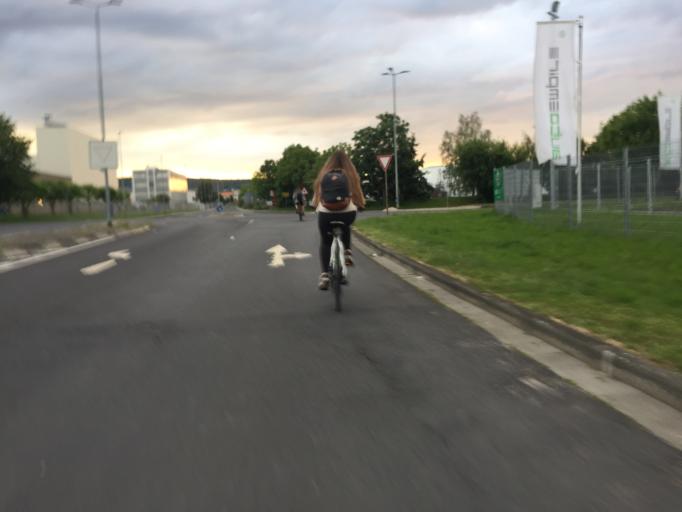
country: DE
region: Hesse
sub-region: Regierungsbezirk Darmstadt
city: Butzbach
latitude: 50.4323
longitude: 8.6866
